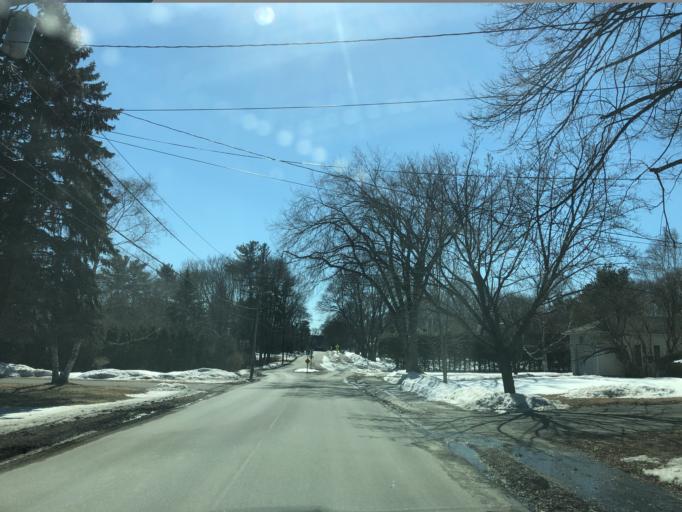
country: US
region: Maine
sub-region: Penobscot County
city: Brewer
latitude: 44.8149
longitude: -68.7535
